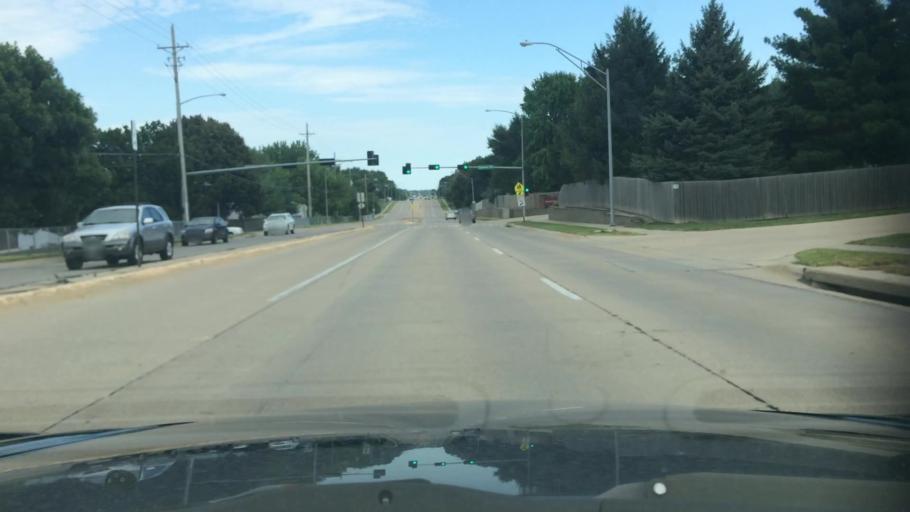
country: US
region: Nebraska
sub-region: Sarpy County
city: La Vista
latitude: 41.1763
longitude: -96.0400
